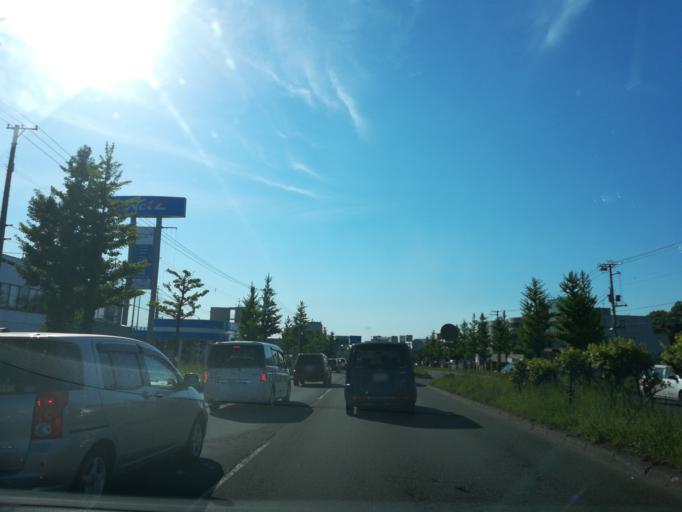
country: JP
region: Hokkaido
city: Kitahiroshima
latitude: 43.0211
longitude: 141.4739
